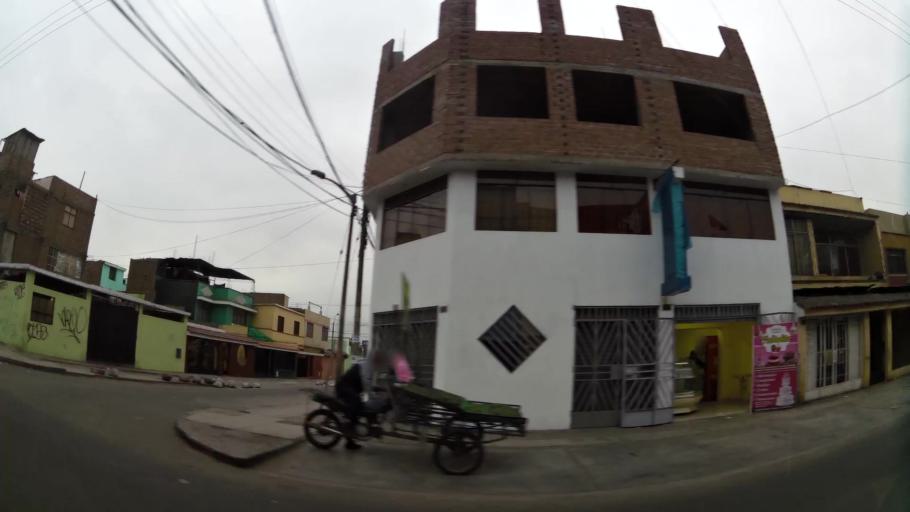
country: PE
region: Lima
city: Lima
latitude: -12.0242
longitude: -76.9861
